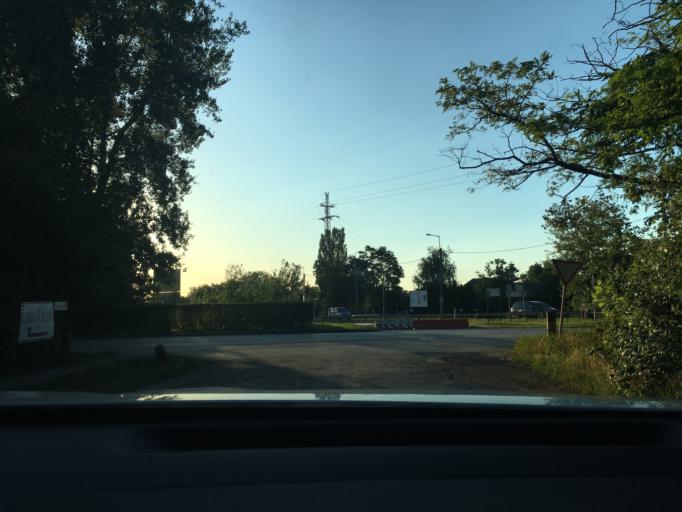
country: HU
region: Budapest
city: Budapest XVII. keruelet
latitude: 47.4714
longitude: 19.2799
